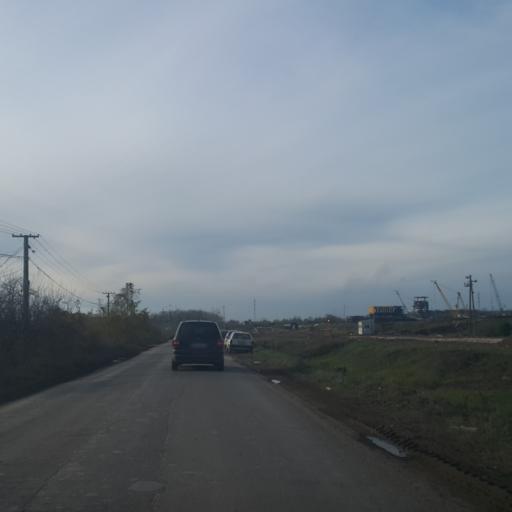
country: RS
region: Central Serbia
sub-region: Belgrade
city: Lazarevac
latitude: 44.4006
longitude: 20.3631
